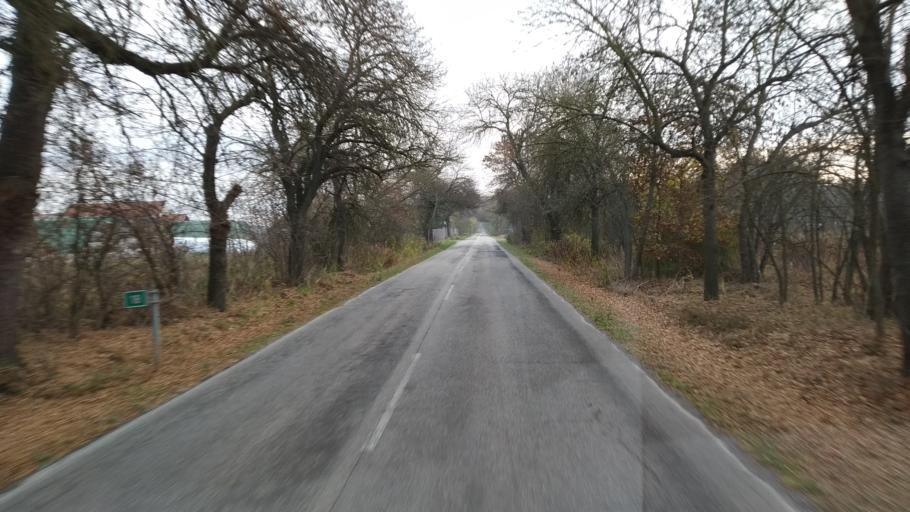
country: HU
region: Pest
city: Dunabogdany
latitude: 47.8000
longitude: 19.0439
